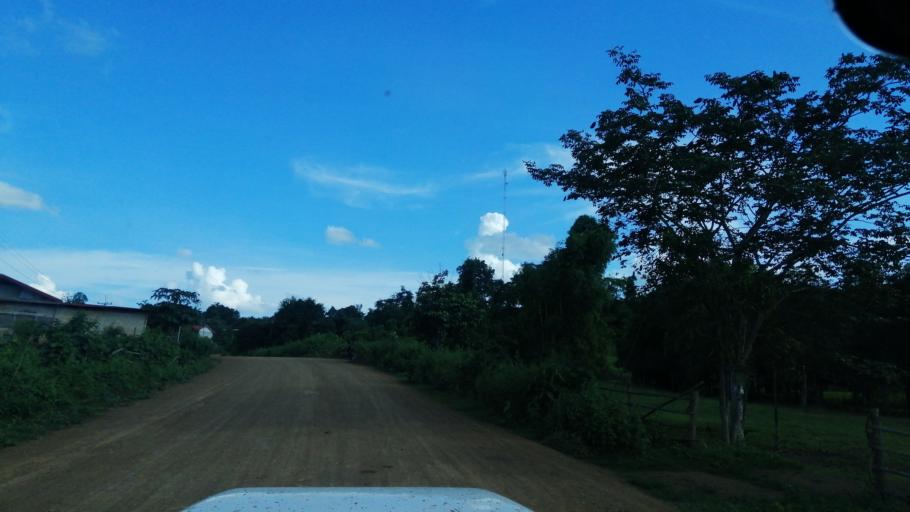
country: LA
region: Xiagnabouli
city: Muang Kenthao
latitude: 17.8473
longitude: 101.2444
